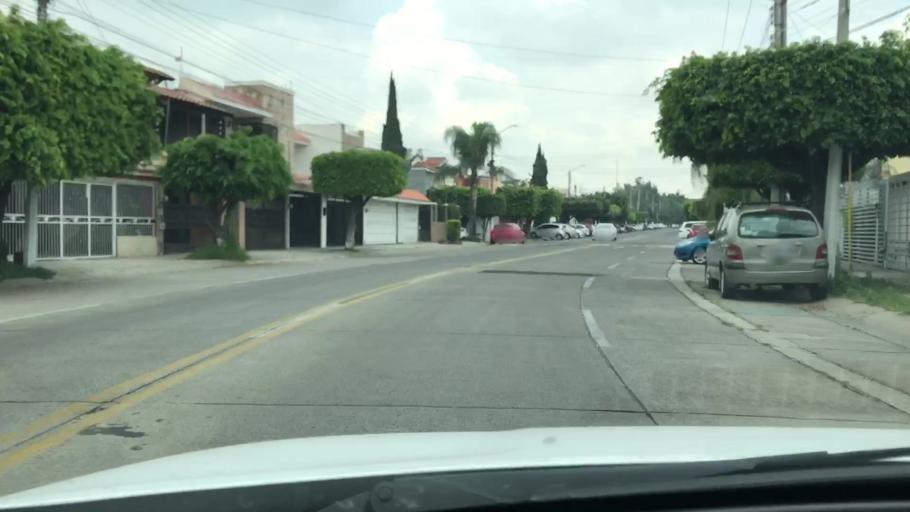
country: MX
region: Jalisco
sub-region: Tlajomulco de Zuniga
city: Palomar
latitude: 20.6345
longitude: -103.4360
